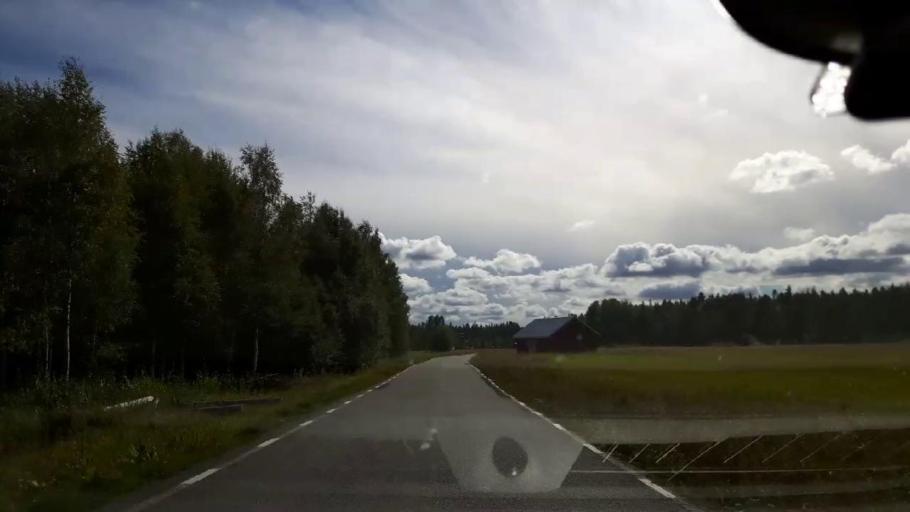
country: SE
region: Jaemtland
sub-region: Braecke Kommun
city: Braecke
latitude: 63.2102
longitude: 15.3496
